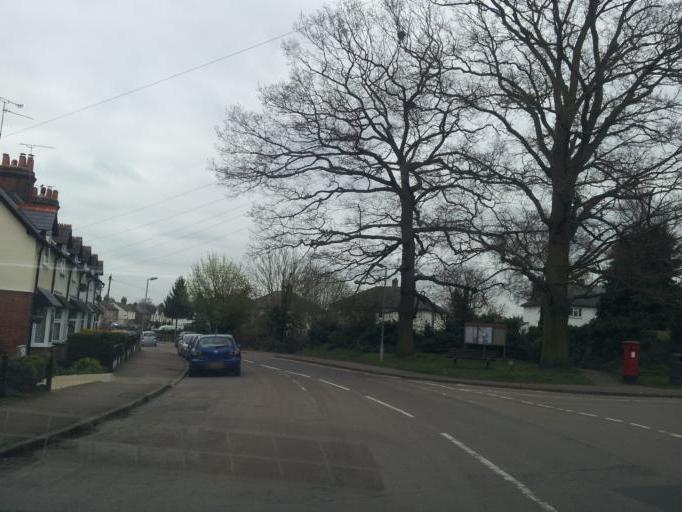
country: GB
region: England
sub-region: Hertfordshire
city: Great Munden
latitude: 51.8889
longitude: 0.0162
